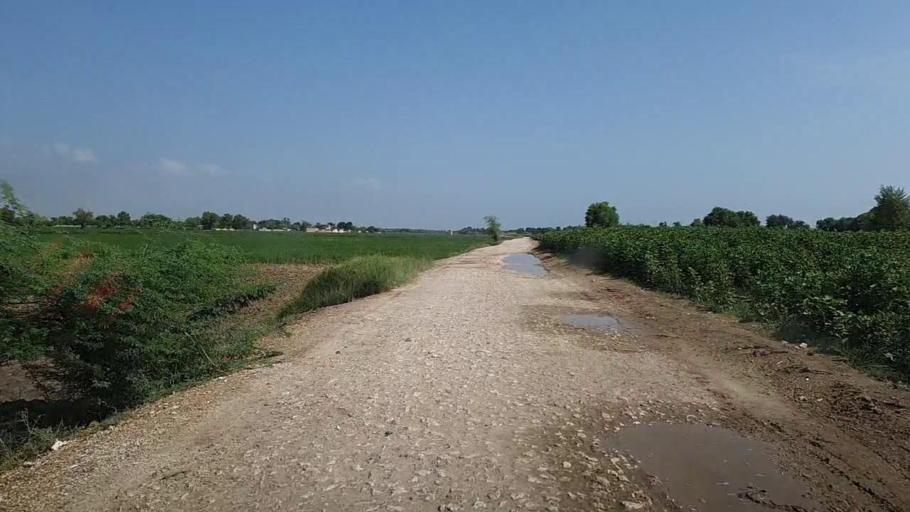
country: PK
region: Sindh
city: Bhiria
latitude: 26.8773
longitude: 68.2303
